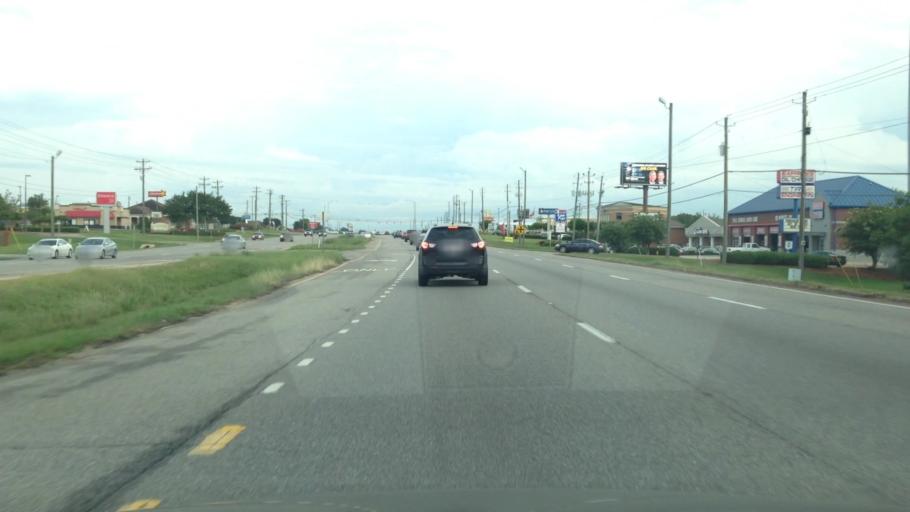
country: US
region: Alabama
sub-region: Montgomery County
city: Pike Road
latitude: 32.3427
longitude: -86.1795
